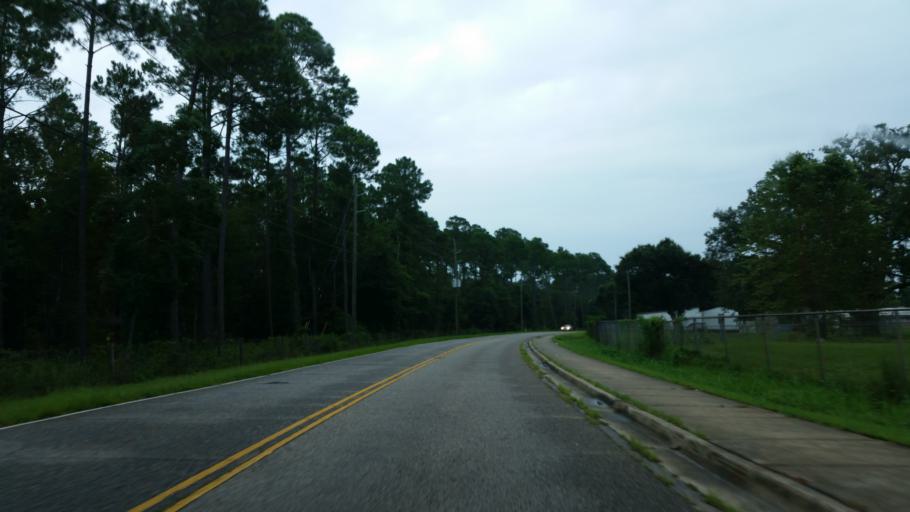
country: US
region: Florida
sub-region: Escambia County
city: Warrington
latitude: 30.3928
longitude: -87.2876
